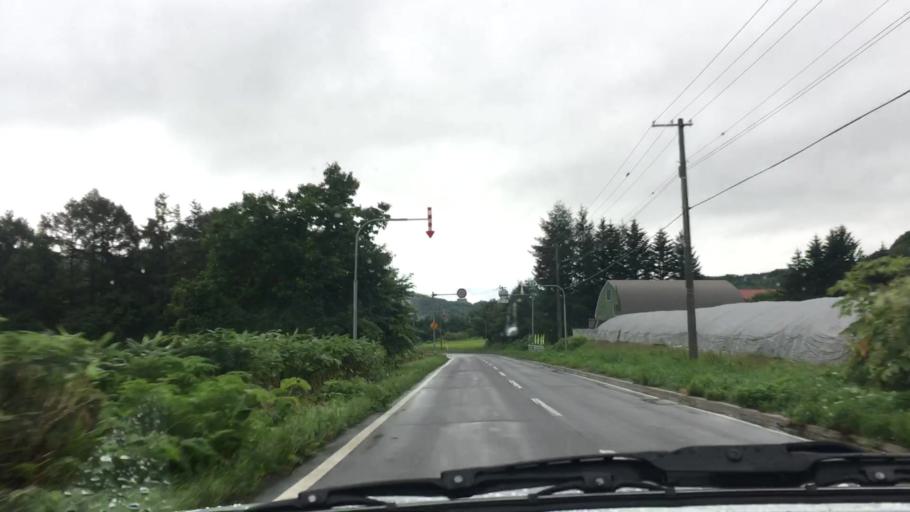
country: JP
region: Hokkaido
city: Niseko Town
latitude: 42.6534
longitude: 140.7394
